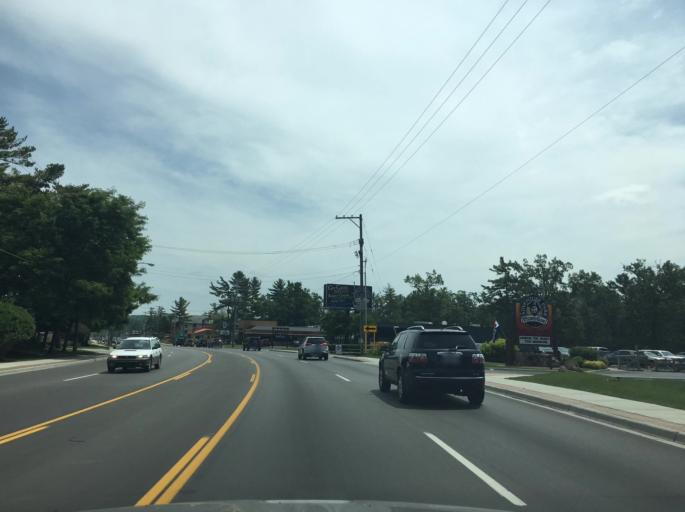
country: US
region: Michigan
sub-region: Grand Traverse County
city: Traverse City
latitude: 44.7457
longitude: -85.5424
